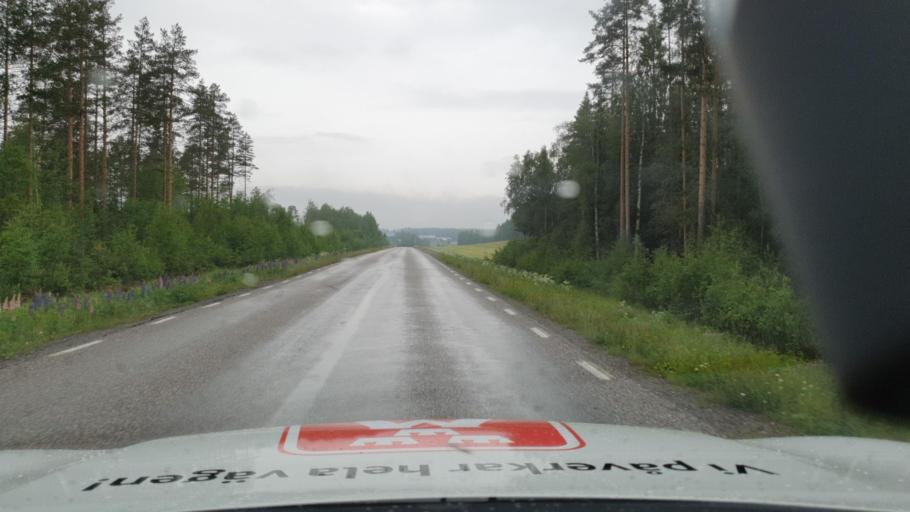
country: SE
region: Vaesterbotten
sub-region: Vannas Kommun
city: Vaennaes
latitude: 63.7851
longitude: 19.5815
